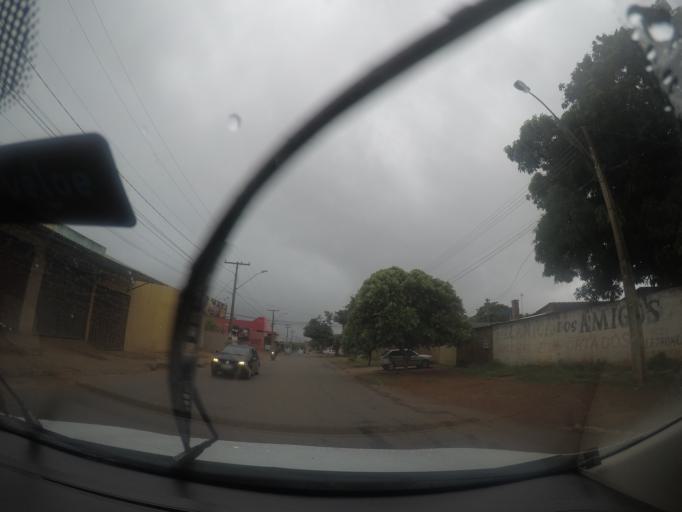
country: BR
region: Goias
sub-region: Goiania
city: Goiania
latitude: -16.6168
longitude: -49.3570
